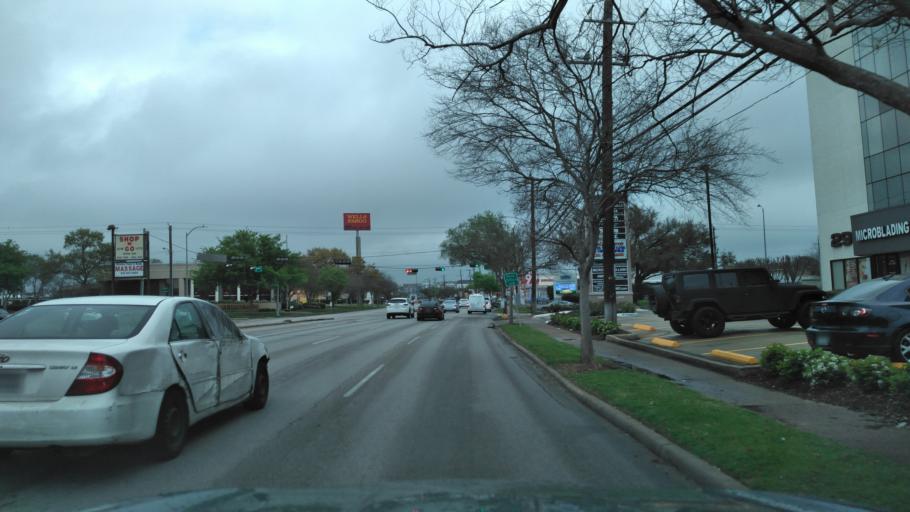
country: US
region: Texas
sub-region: Harris County
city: Piney Point Village
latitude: 29.7342
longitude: -95.5011
